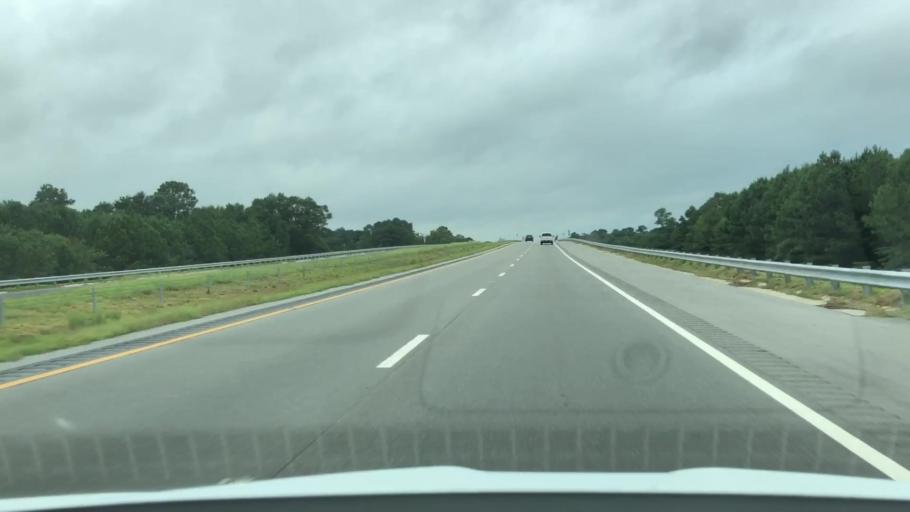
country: US
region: North Carolina
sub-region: Wayne County
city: Elroy
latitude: 35.3392
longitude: -77.8444
